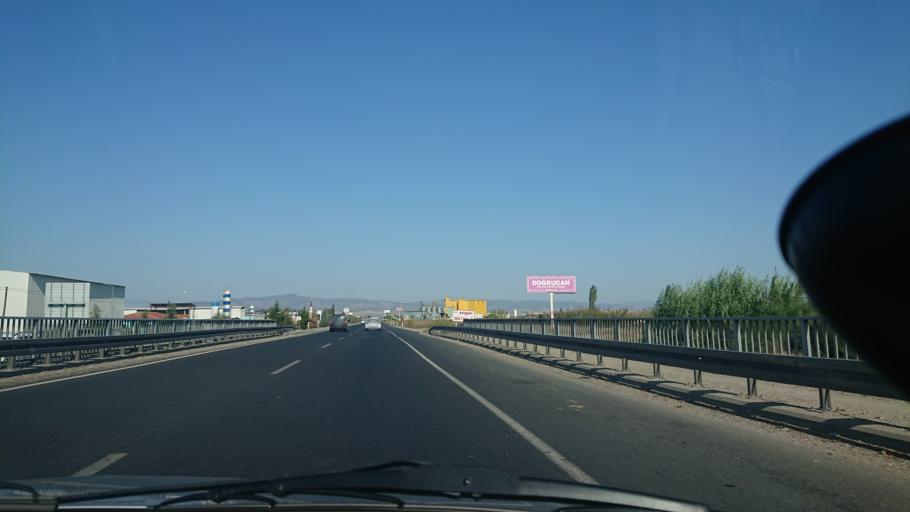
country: TR
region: Manisa
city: Salihli
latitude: 38.5026
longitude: 28.2154
